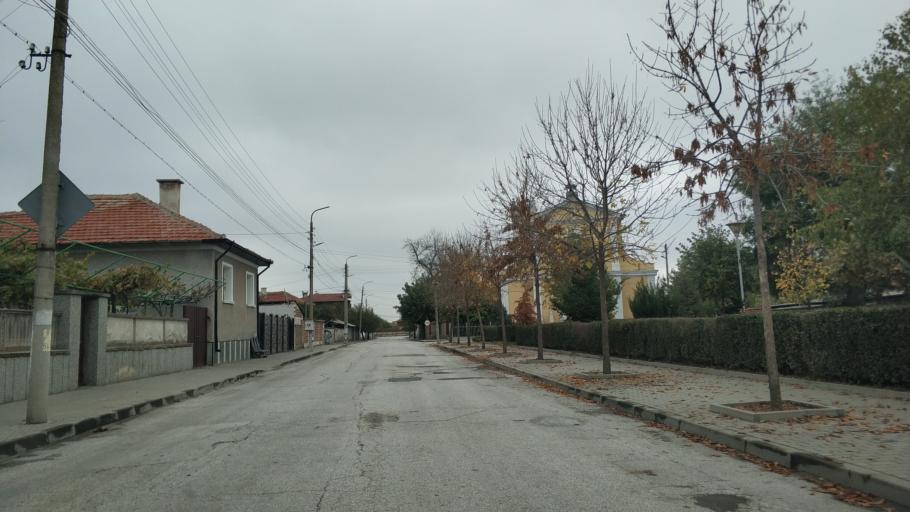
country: BG
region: Plovdiv
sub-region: Obshtina Kaloyanovo
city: Kaloyanovo
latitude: 42.3704
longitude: 24.7206
